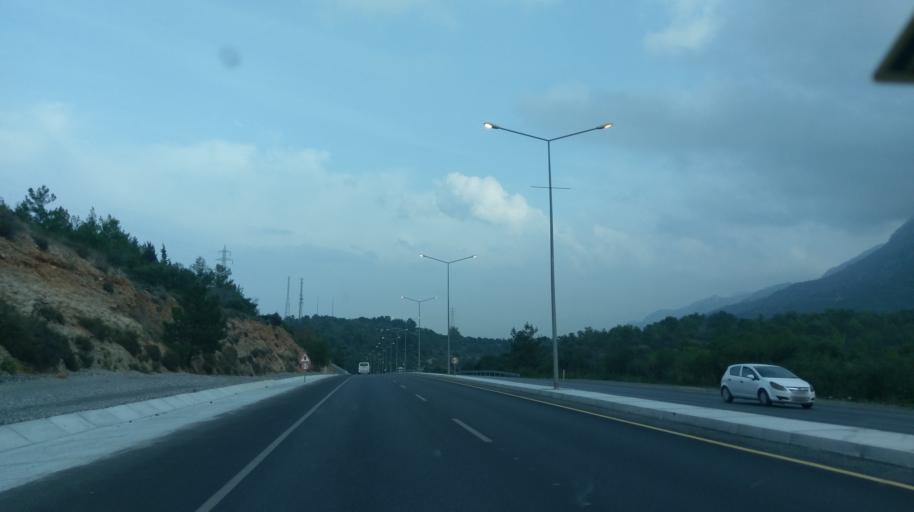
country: CY
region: Keryneia
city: Kyrenia
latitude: 35.3088
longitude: 33.3111
